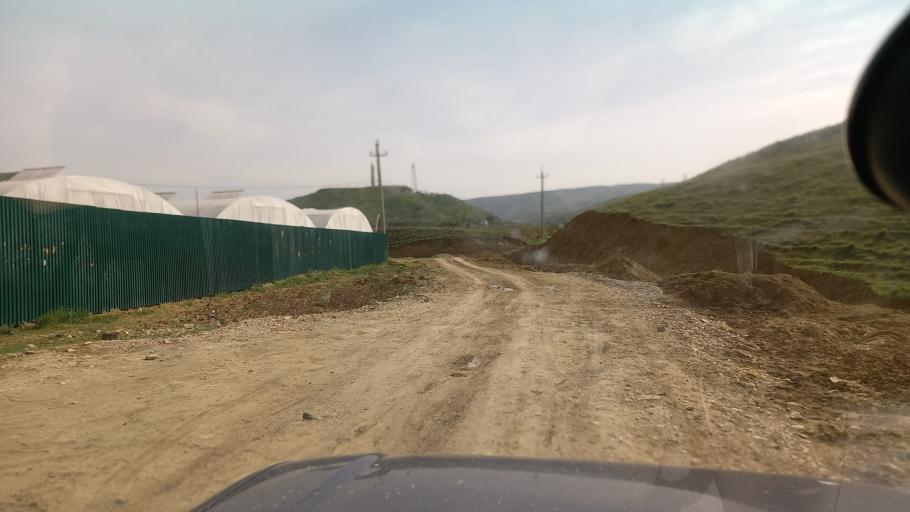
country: RU
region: Dagestan
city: Karabudakhkent
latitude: 42.7175
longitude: 47.5671
